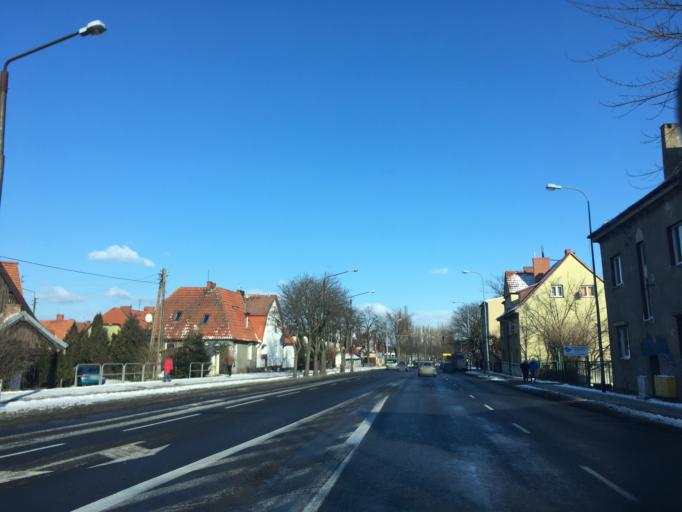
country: PL
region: Pomeranian Voivodeship
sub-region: Powiat slupski
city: Kobylnica
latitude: 54.4607
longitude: 17.0020
